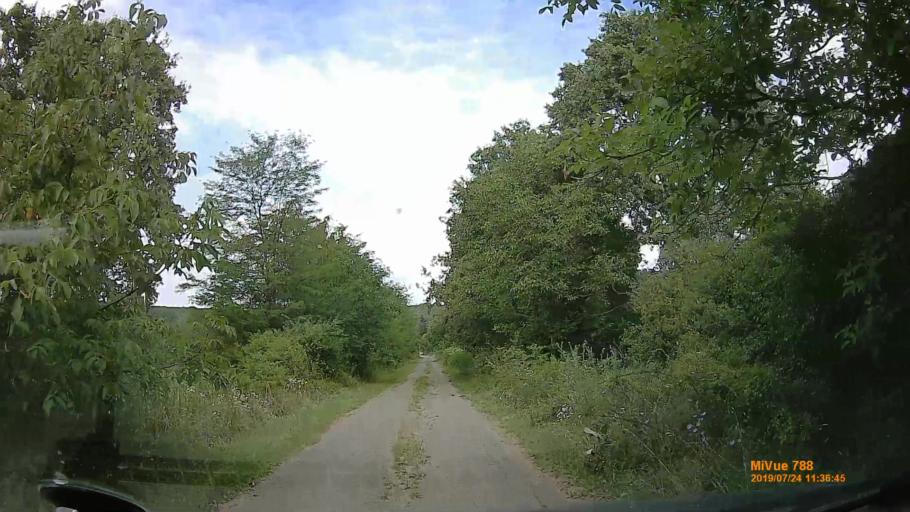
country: UA
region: Zakarpattia
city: Batiovo
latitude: 48.2400
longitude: 22.4767
